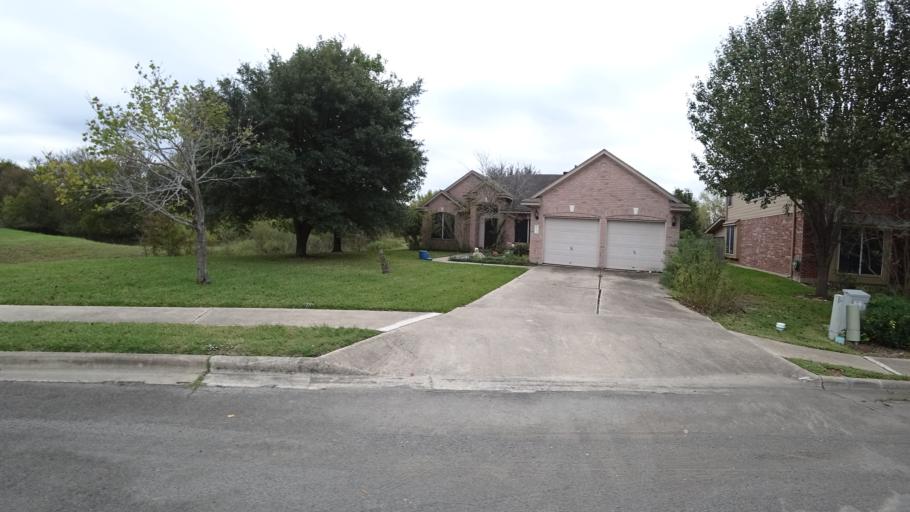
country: US
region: Texas
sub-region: Travis County
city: Shady Hollow
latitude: 30.1518
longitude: -97.8548
